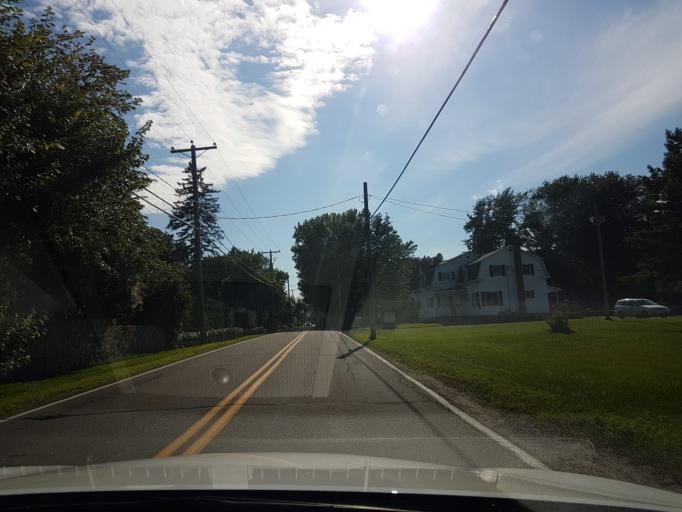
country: CA
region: Quebec
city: Sainte-Catherine
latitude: 46.2917
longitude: -72.6276
